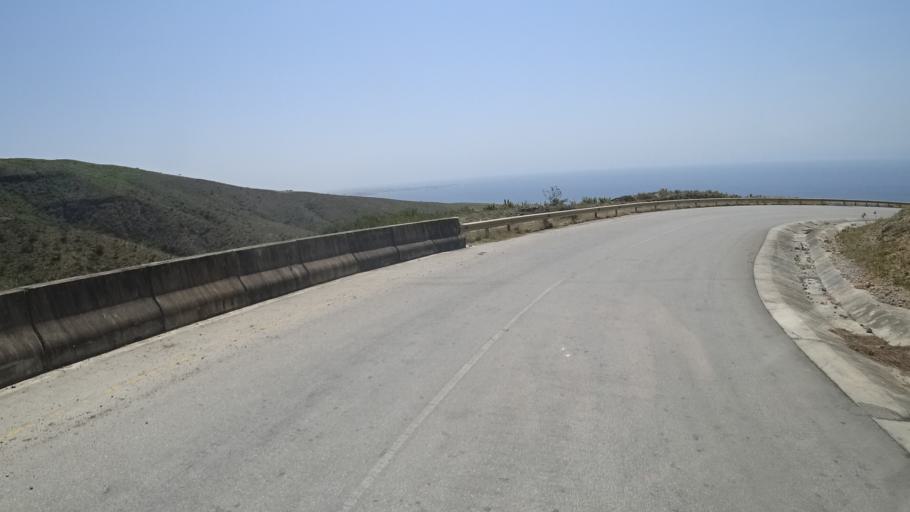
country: OM
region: Zufar
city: Salalah
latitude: 17.0498
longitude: 54.6124
